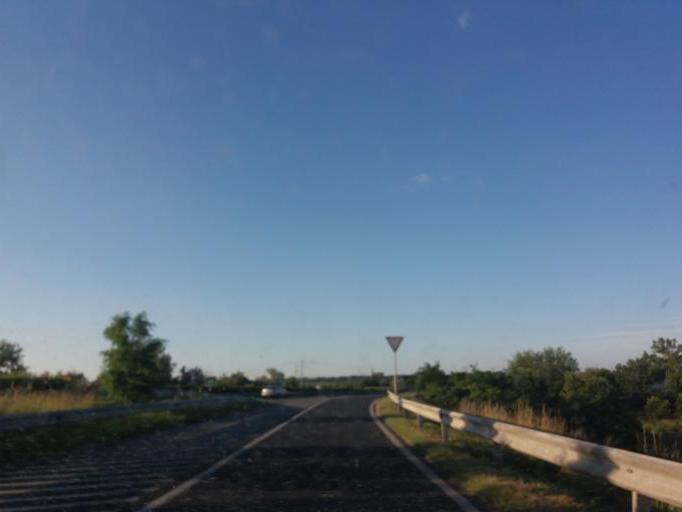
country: HU
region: Fejer
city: Martonvasar
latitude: 47.3310
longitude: 18.7777
